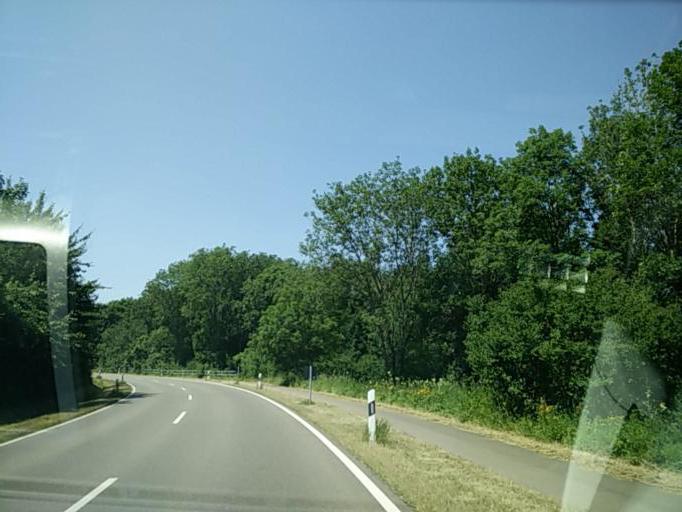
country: DE
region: Baden-Wuerttemberg
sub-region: Tuebingen Region
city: Gomaringen
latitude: 48.4300
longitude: 9.1245
